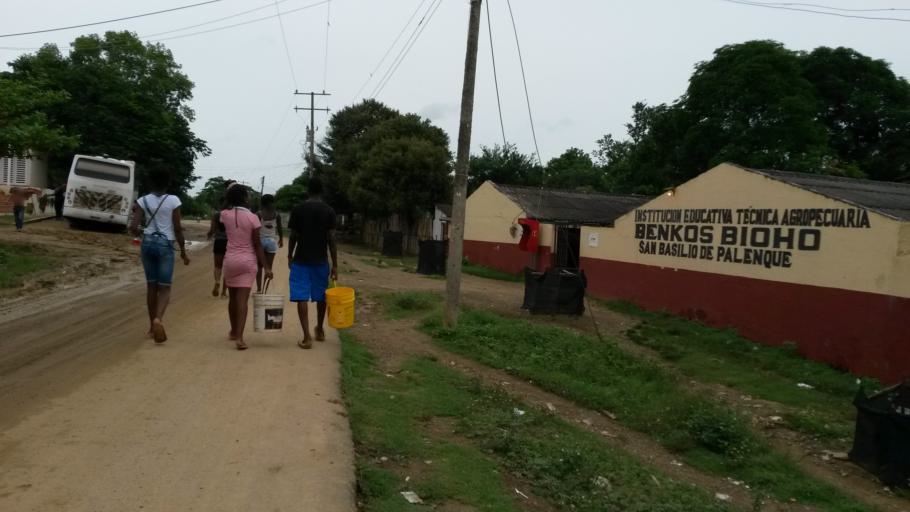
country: CO
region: Bolivar
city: San Pablo
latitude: 10.1068
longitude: -75.2008
